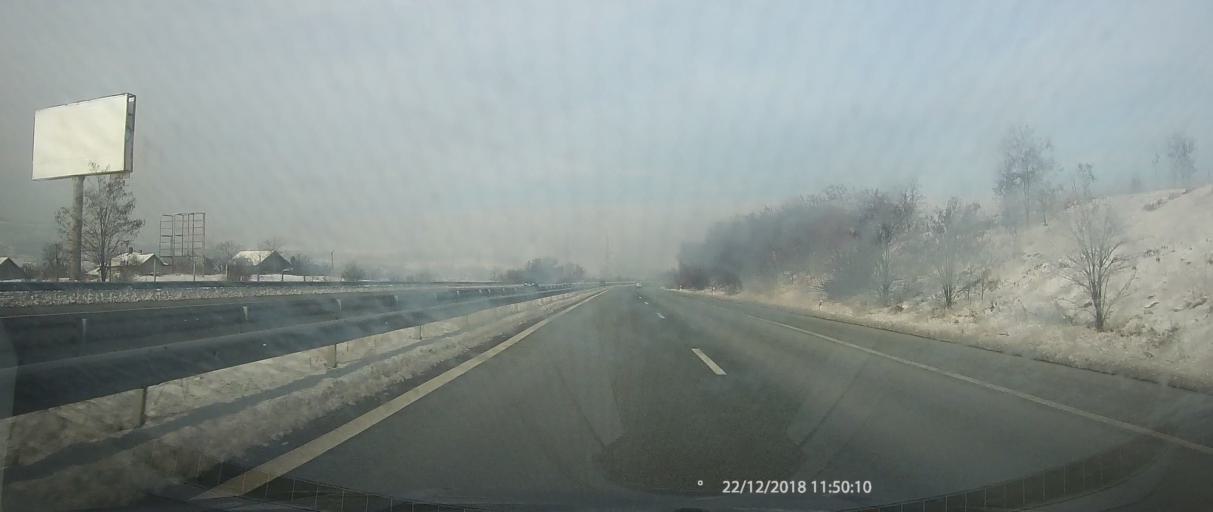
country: BG
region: Pernik
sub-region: Obshtina Pernik
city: Pernik
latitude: 42.5593
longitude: 23.1173
